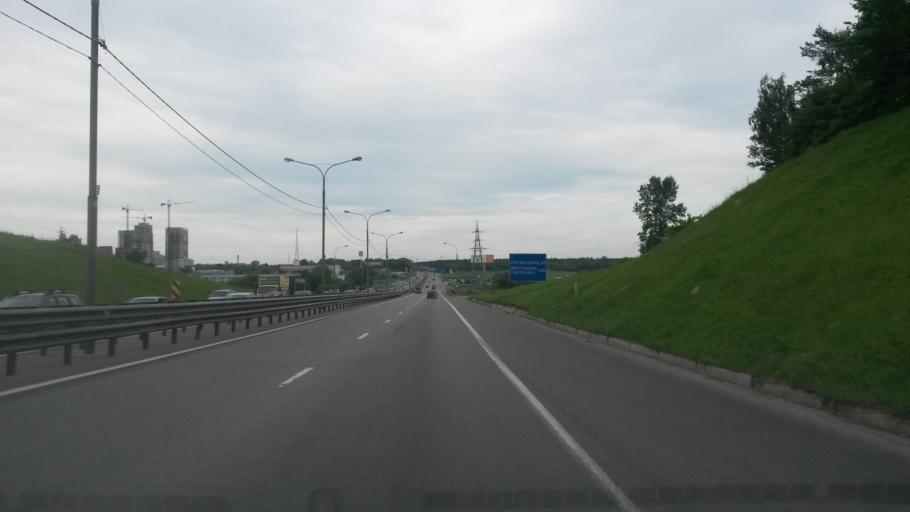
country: RU
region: Moskovskaya
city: Lesnyye Polyany
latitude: 55.9882
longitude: 37.8723
